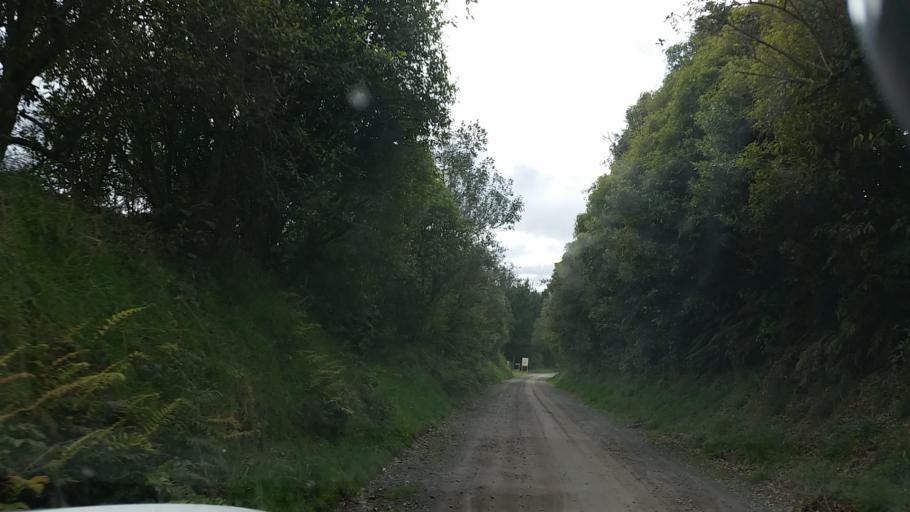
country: NZ
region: Bay of Plenty
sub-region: Rotorua District
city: Rotorua
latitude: -38.2420
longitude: 176.3451
